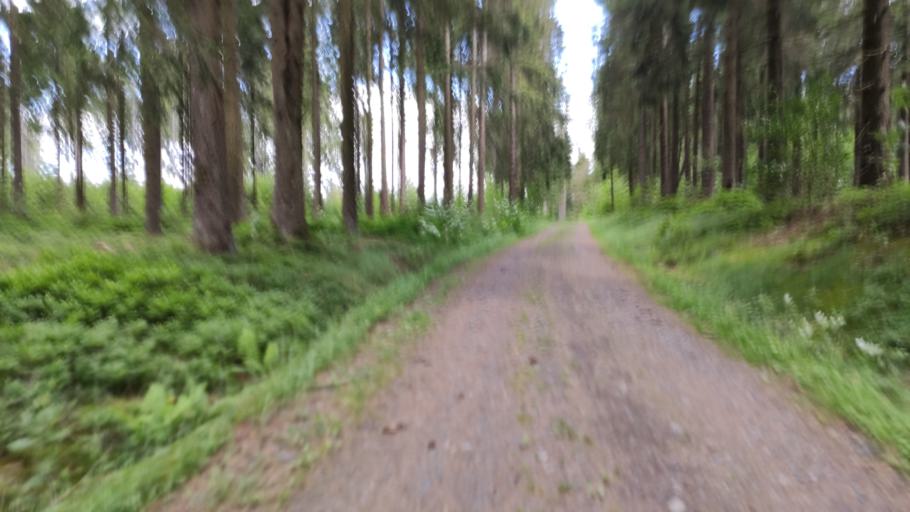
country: DE
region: Bavaria
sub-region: Upper Franconia
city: Tschirn
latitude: 50.4291
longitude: 11.4748
